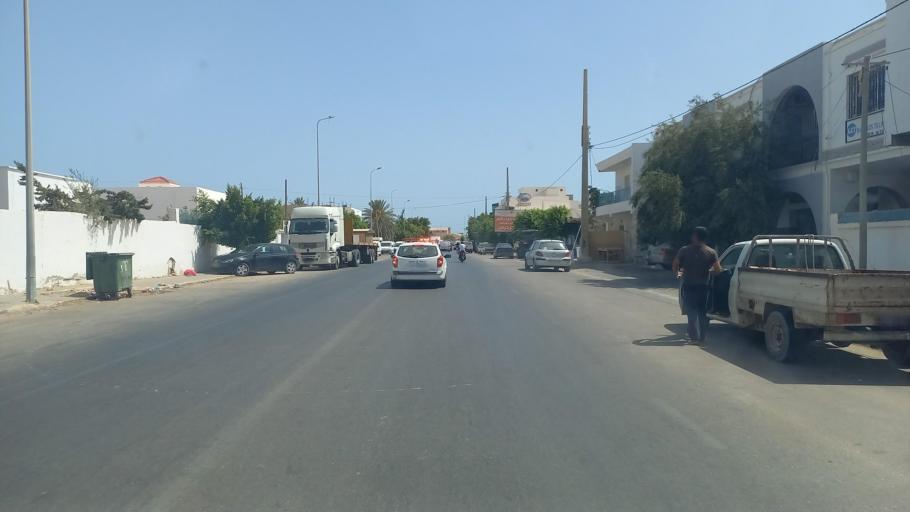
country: TN
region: Madanin
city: Zarzis
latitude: 33.4970
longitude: 11.0893
